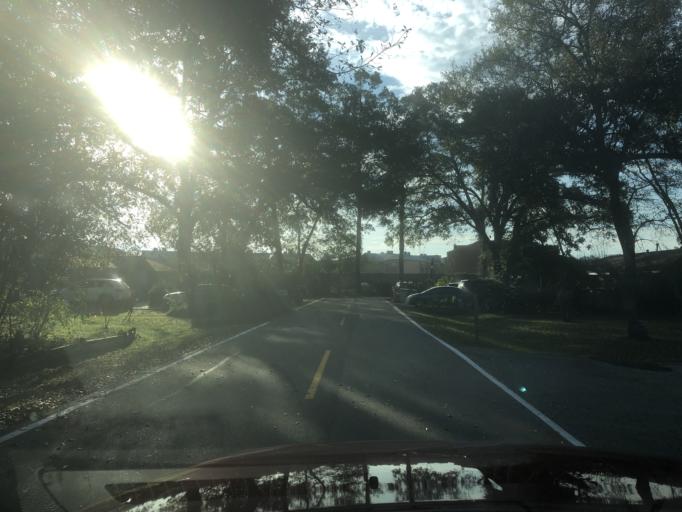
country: US
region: Texas
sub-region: Harris County
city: Spring
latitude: 30.0085
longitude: -95.4688
